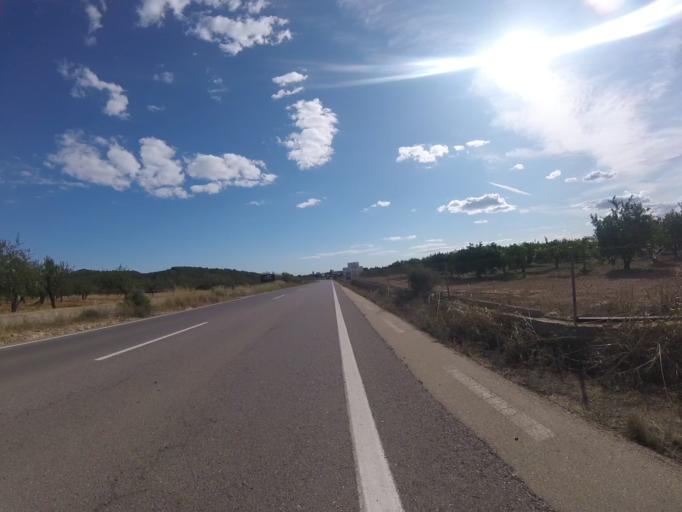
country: ES
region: Valencia
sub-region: Provincia de Castello
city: Alcoceber
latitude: 40.2597
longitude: 0.2438
